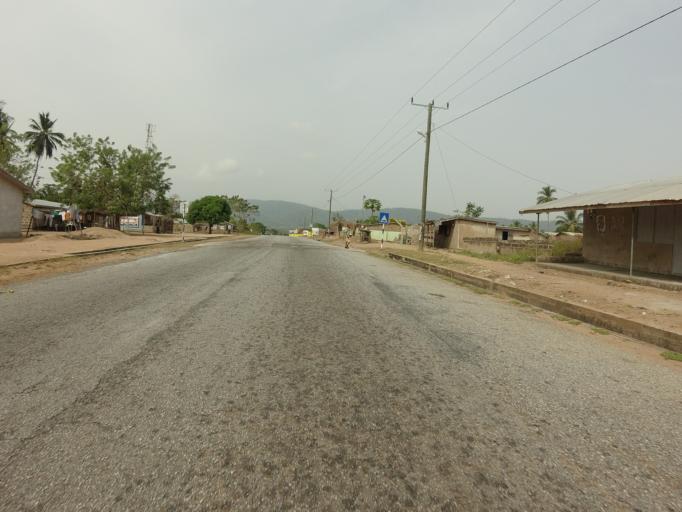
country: GH
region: Volta
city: Ho
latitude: 6.5759
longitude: 0.3335
